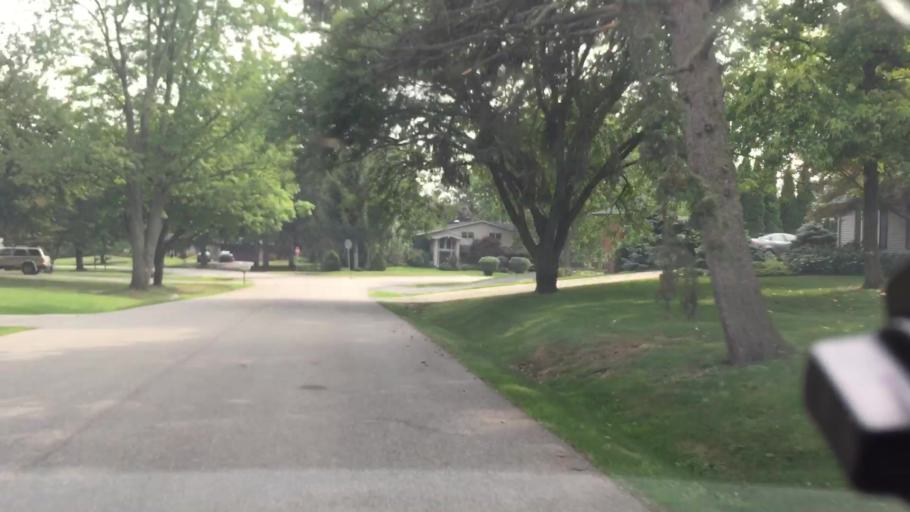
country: US
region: Michigan
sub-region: Oakland County
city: Sylvan Lake
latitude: 42.6010
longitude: -83.2930
